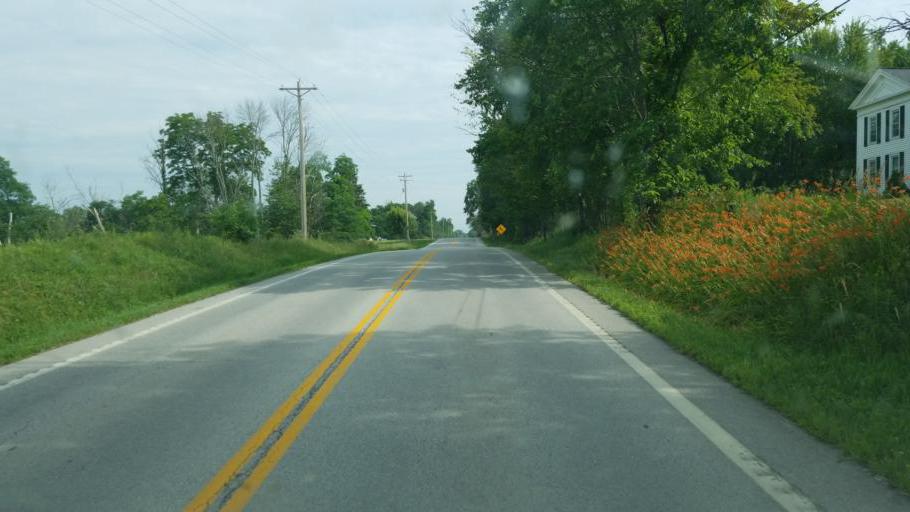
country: US
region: Ohio
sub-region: Medina County
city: Lodi
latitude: 41.1182
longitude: -82.0241
